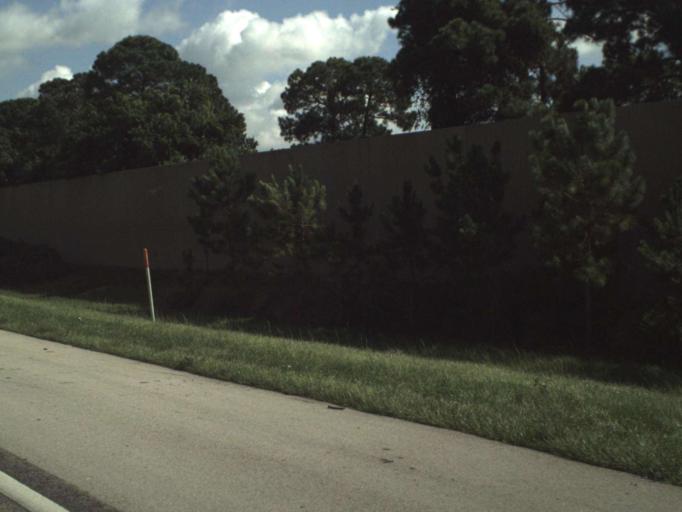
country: US
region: Florida
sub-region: Palm Beach County
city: Limestone Creek
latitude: 26.8914
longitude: -80.1329
